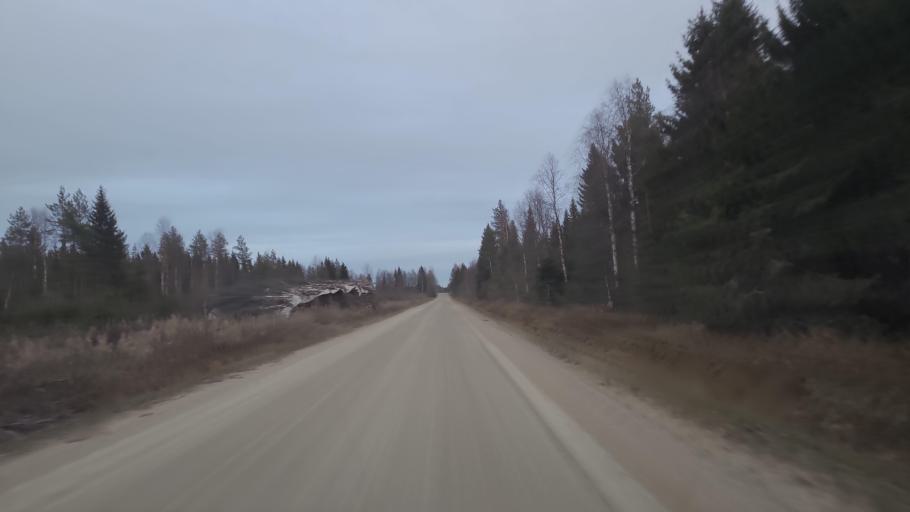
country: FI
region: Lapland
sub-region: Kemi-Tornio
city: Tervola
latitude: 66.0731
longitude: 24.8561
